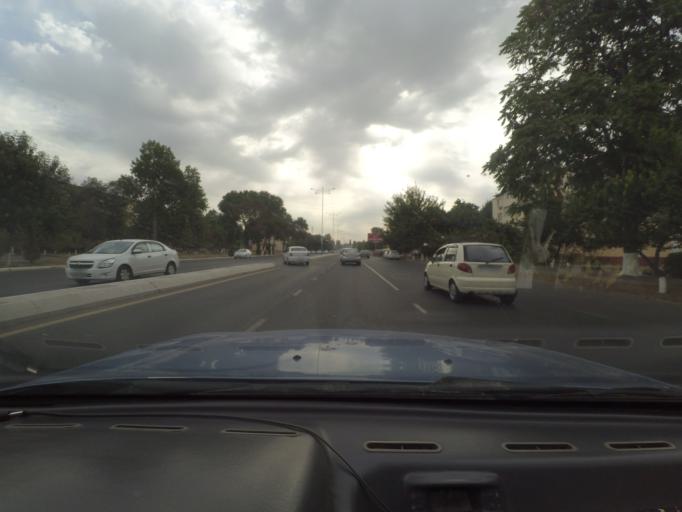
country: UZ
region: Toshkent
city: Salor
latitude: 41.3547
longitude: 69.3646
